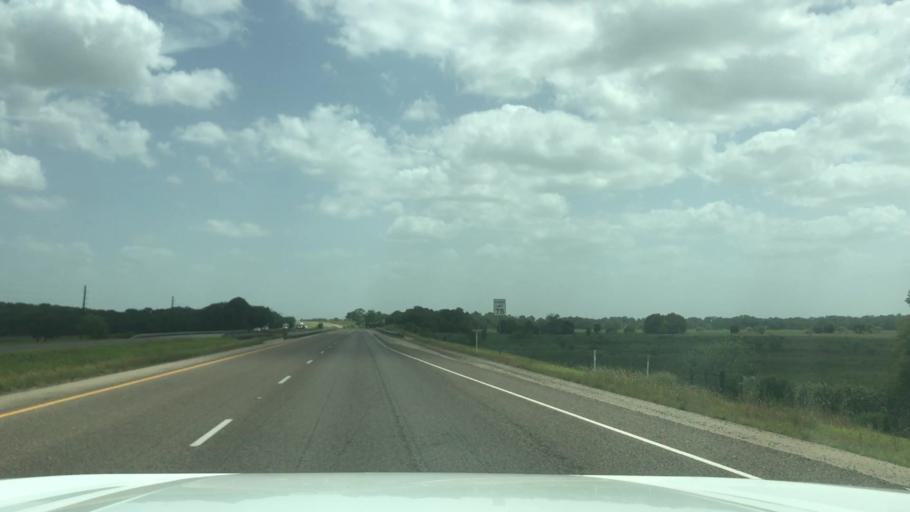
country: US
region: Texas
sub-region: Robertson County
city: Calvert
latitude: 31.0165
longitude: -96.7058
